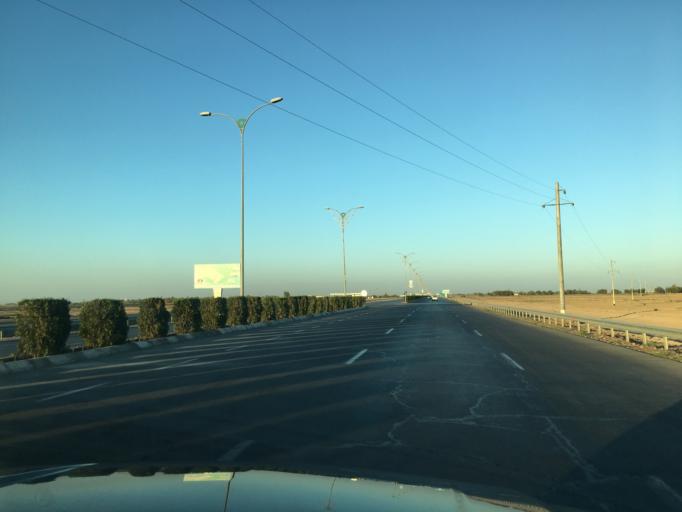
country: TM
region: Dasoguz
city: Dasoguz
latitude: 41.7823
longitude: 59.8594
